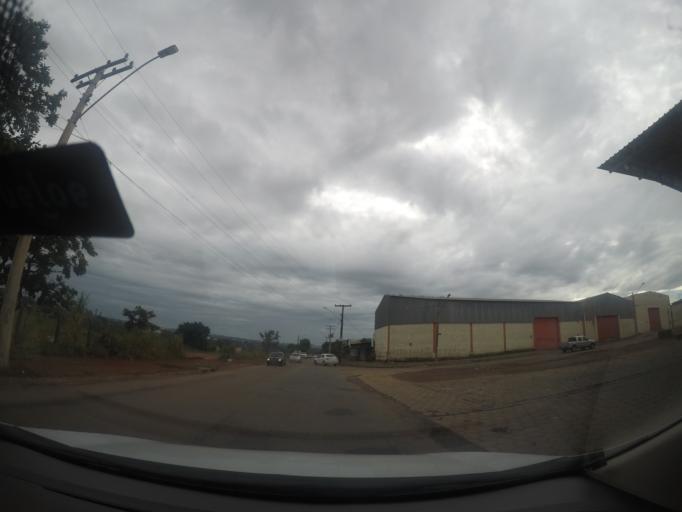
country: BR
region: Goias
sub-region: Goiania
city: Goiania
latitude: -16.6447
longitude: -49.3378
